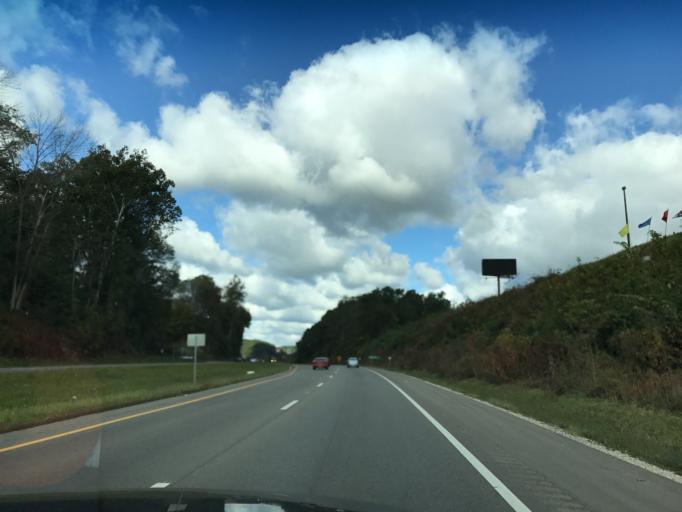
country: US
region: Ohio
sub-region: Fairfield County
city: Geneva
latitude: 39.5840
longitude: -82.5263
